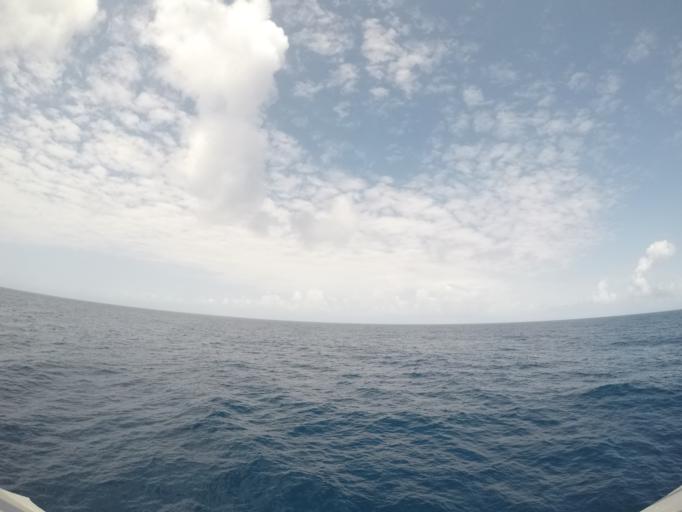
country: TZ
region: Zanzibar North
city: Nungwi
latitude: -5.5719
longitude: 39.3672
